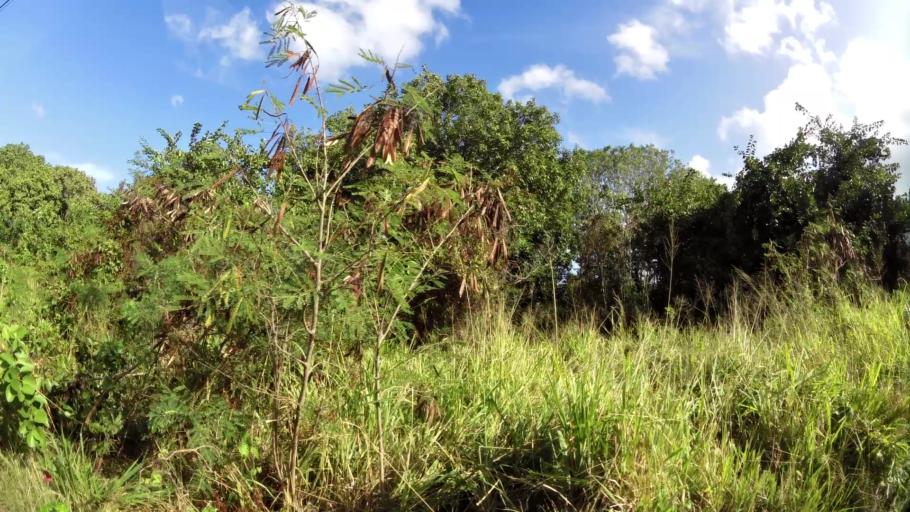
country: KN
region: Saint Paul Charlestown
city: Charlestown
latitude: 17.1451
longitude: -62.6264
